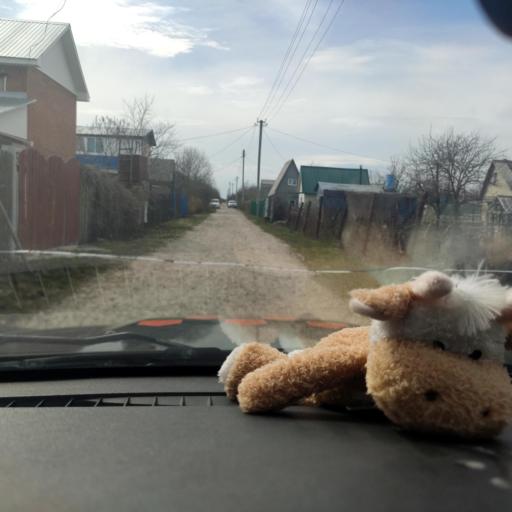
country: RU
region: Samara
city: Podstepki
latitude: 53.5945
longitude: 49.2337
